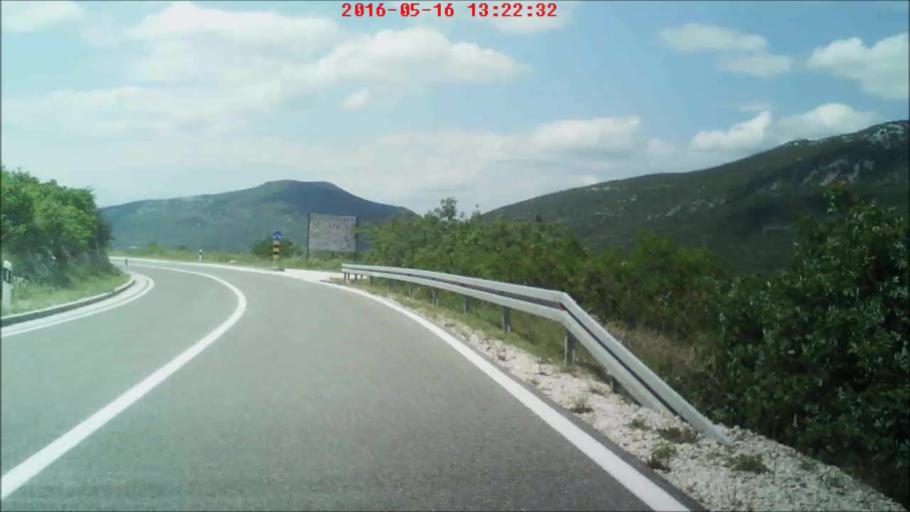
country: HR
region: Dubrovacko-Neretvanska
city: Ston
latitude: 42.8354
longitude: 17.7213
